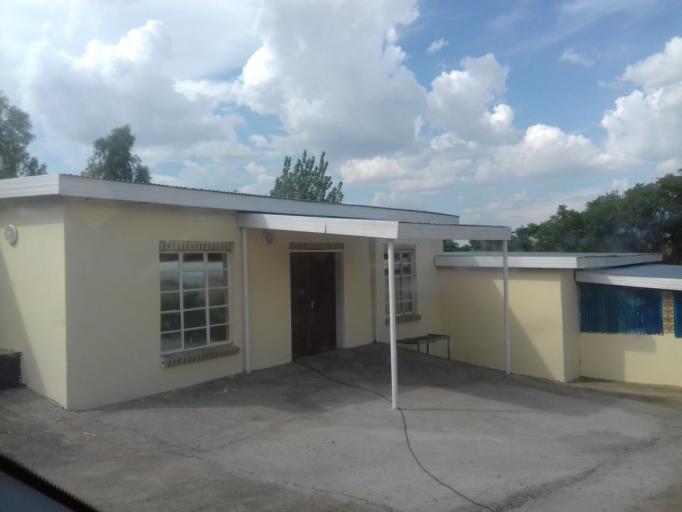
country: LS
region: Mafeteng
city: Mafeteng
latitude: -29.6883
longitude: 27.4343
